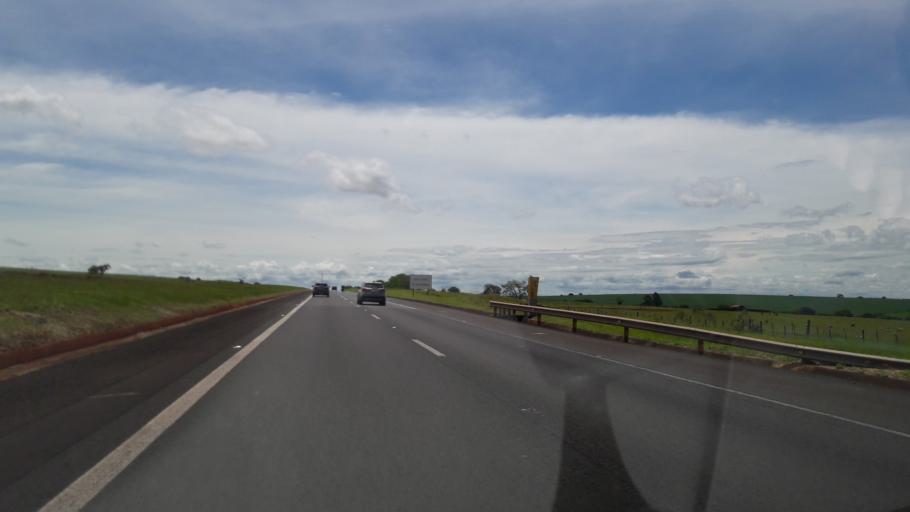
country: BR
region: Sao Paulo
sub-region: Avare
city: Avare
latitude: -22.9560
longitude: -48.8419
